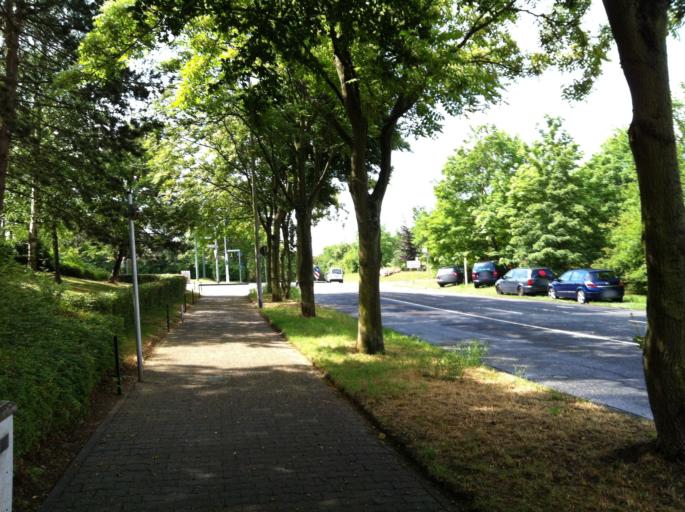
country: DE
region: Rheinland-Pfalz
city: Budenheim
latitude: 49.9964
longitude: 8.1736
